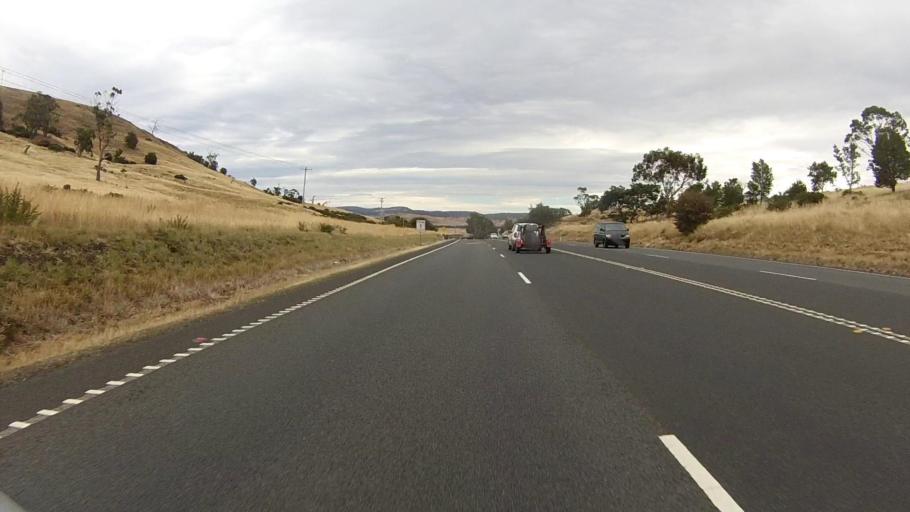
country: AU
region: Tasmania
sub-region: Brighton
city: Bridgewater
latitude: -42.3343
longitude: 147.3434
